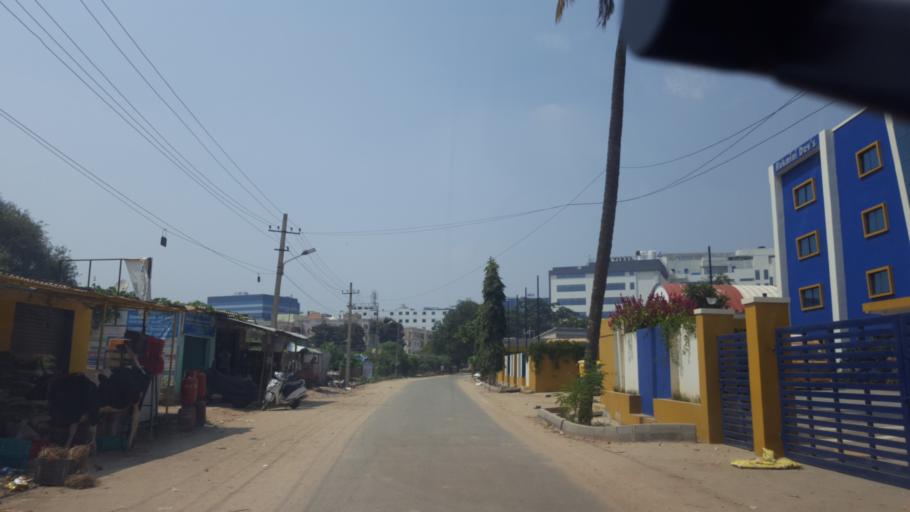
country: IN
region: Karnataka
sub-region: Bangalore Urban
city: Bangalore
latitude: 12.9425
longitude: 77.7007
